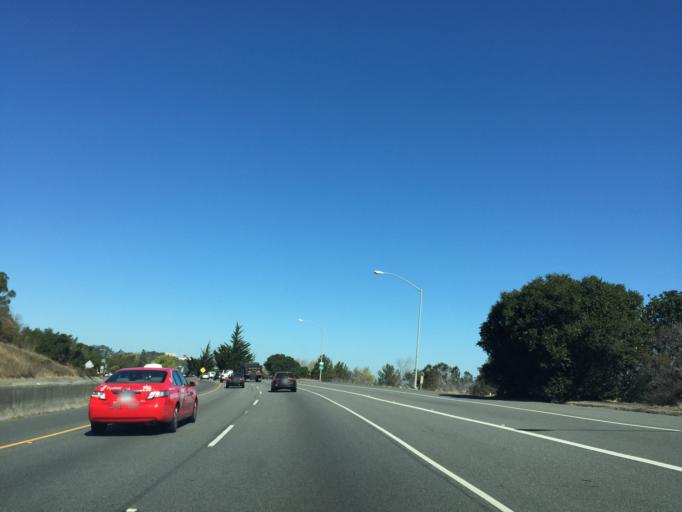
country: US
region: California
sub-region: San Mateo County
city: Highlands-Baywood Park
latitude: 37.5154
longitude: -122.3289
